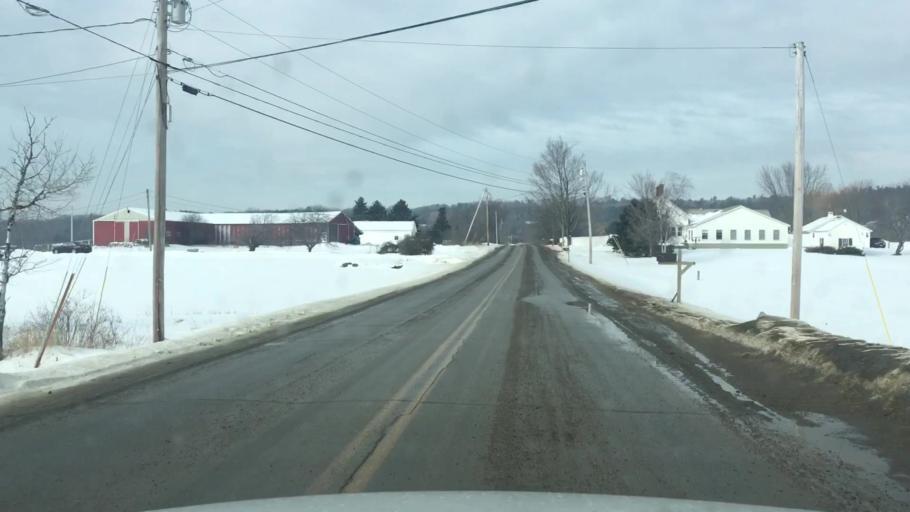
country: US
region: Maine
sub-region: Penobscot County
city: Hermon
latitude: 44.7641
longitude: -68.9526
